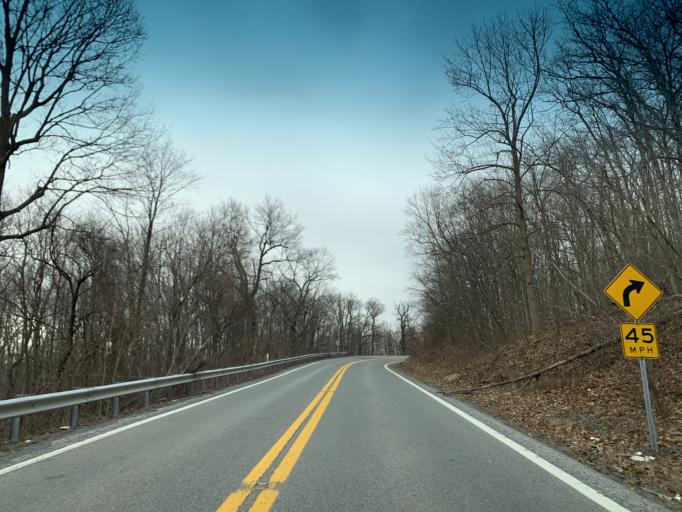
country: US
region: West Virginia
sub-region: Jefferson County
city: Shannondale
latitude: 39.2595
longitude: -77.7727
